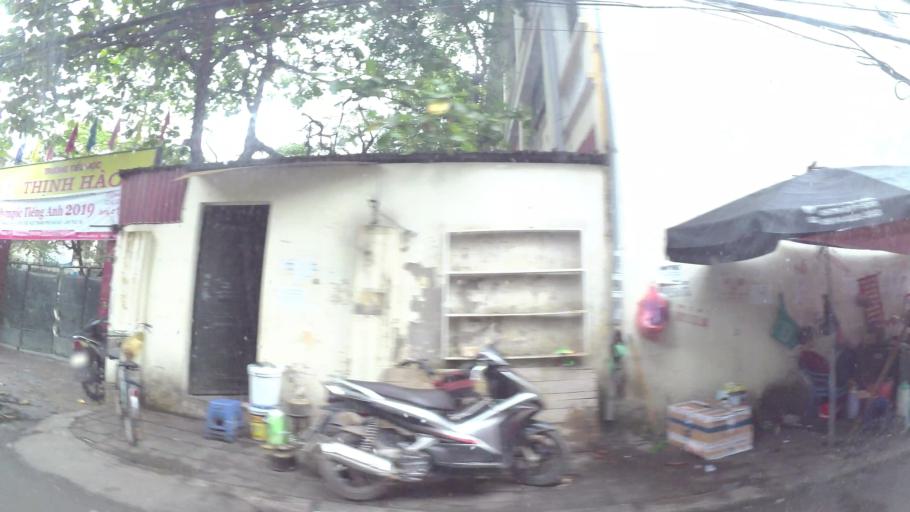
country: VN
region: Ha Noi
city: Dong Da
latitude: 21.0185
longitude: 105.8287
